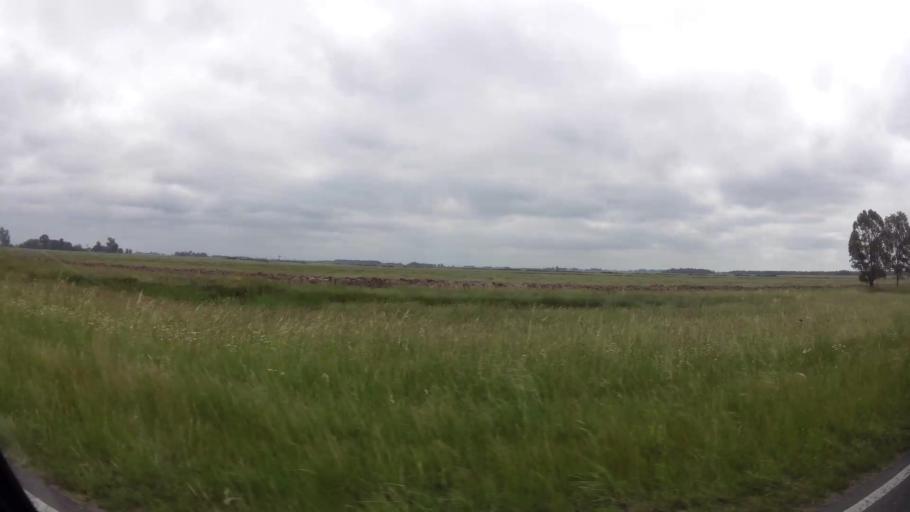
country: AR
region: Buenos Aires
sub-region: Partido de San Vicente
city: San Vicente
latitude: -35.0487
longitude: -58.4489
